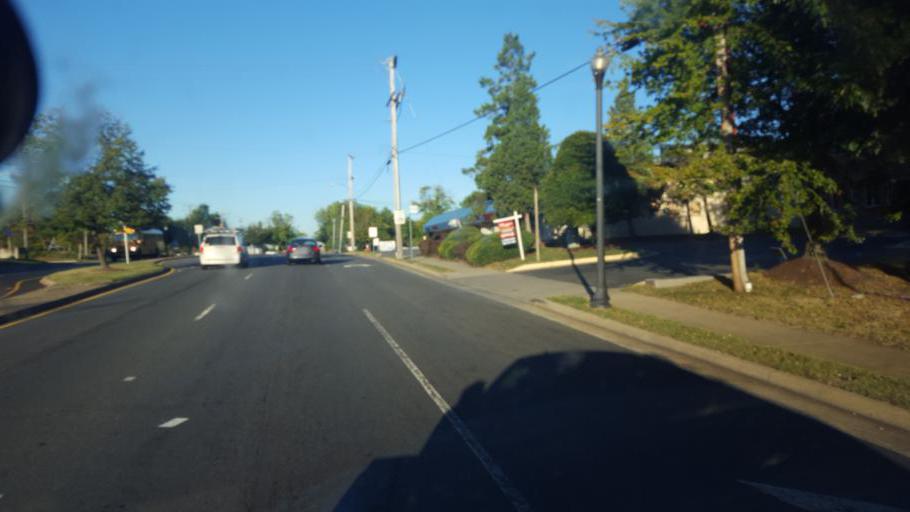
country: US
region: Virginia
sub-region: City of Fairfax
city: Fairfax
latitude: 38.8523
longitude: -77.3281
